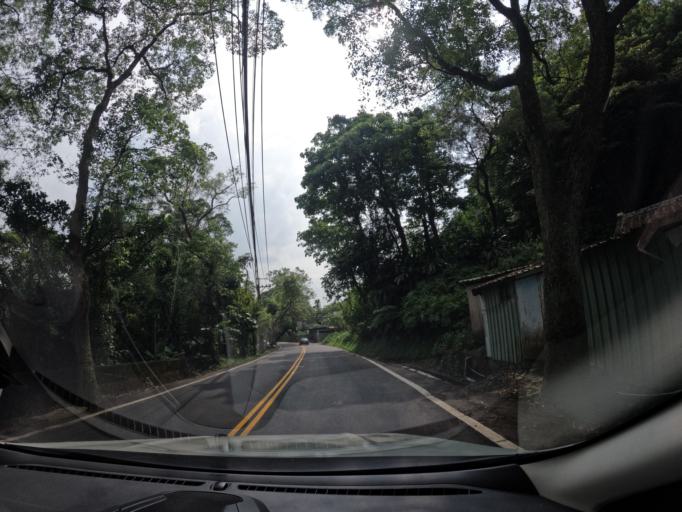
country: TW
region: Taiwan
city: Daxi
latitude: 24.9123
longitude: 121.3825
